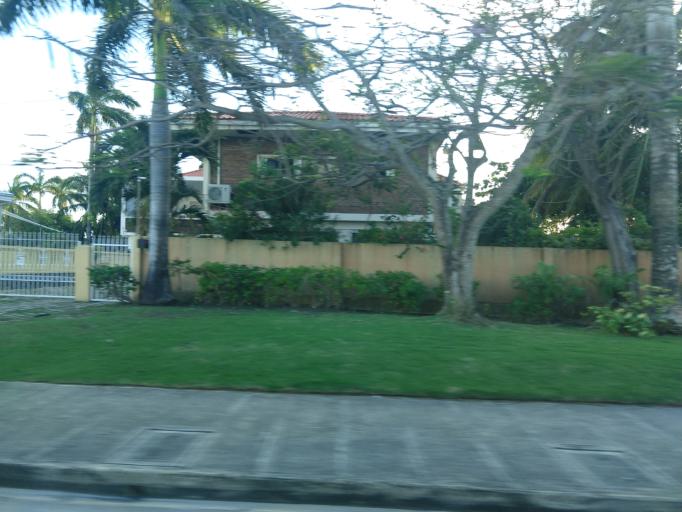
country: BZ
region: Belize
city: Belize City
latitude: 17.5120
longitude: -88.1882
